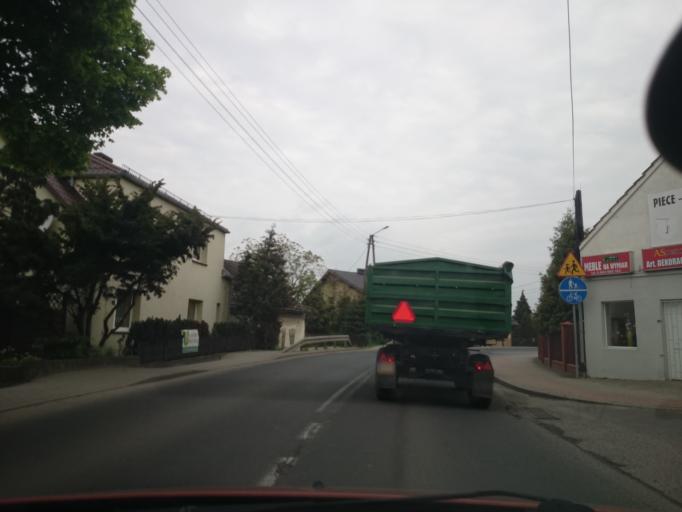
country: PL
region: Opole Voivodeship
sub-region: Powiat opolski
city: Dobrzen Wielki
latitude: 50.7628
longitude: 17.8438
